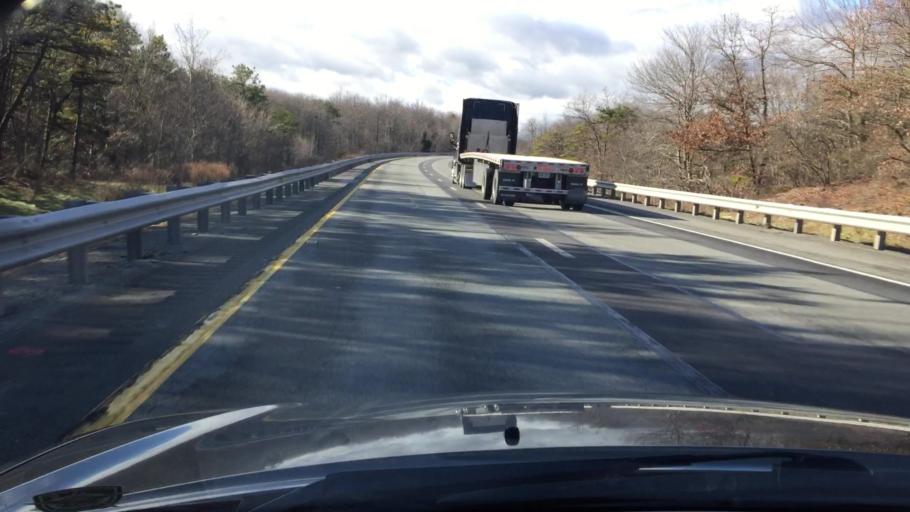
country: US
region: Pennsylvania
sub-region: Monroe County
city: Emerald Lakes
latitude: 41.0734
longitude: -75.4054
